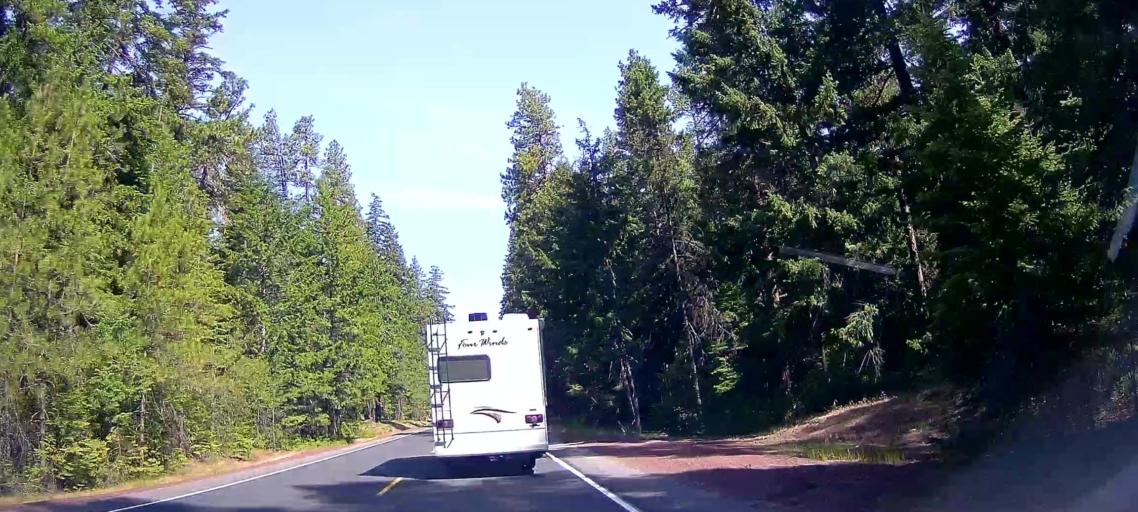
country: US
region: Oregon
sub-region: Jefferson County
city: Warm Springs
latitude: 45.0766
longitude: -121.5375
